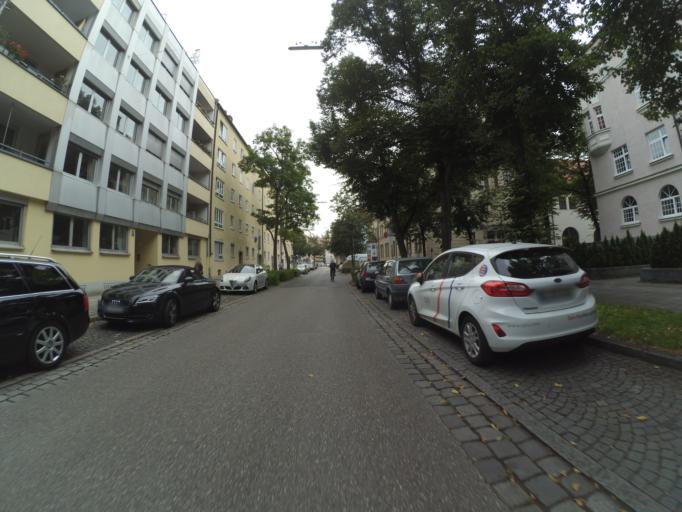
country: DE
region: Bavaria
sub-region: Upper Bavaria
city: Munich
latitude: 48.1620
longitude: 11.5666
